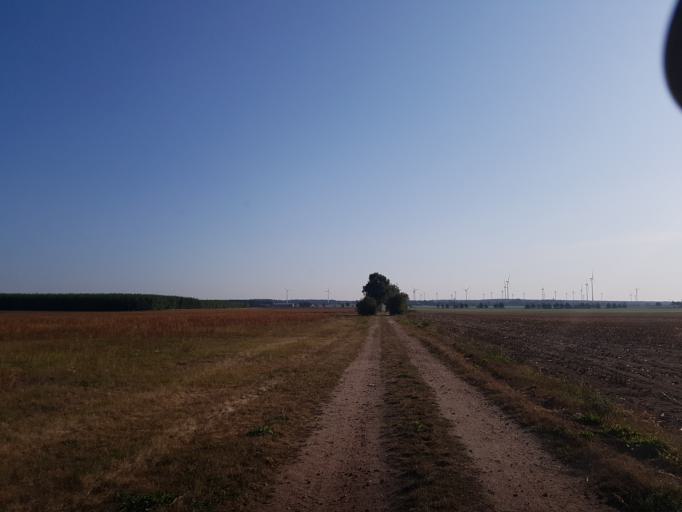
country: DE
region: Brandenburg
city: Finsterwalde
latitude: 51.6243
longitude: 13.7434
